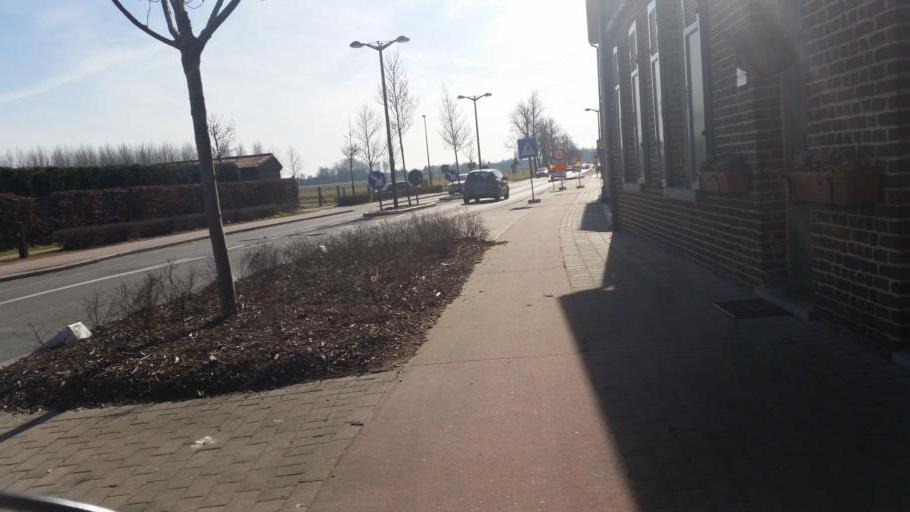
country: BE
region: Flanders
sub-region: Provincie Vlaams-Brabant
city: Steenokkerzeel
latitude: 50.9307
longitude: 4.4985
